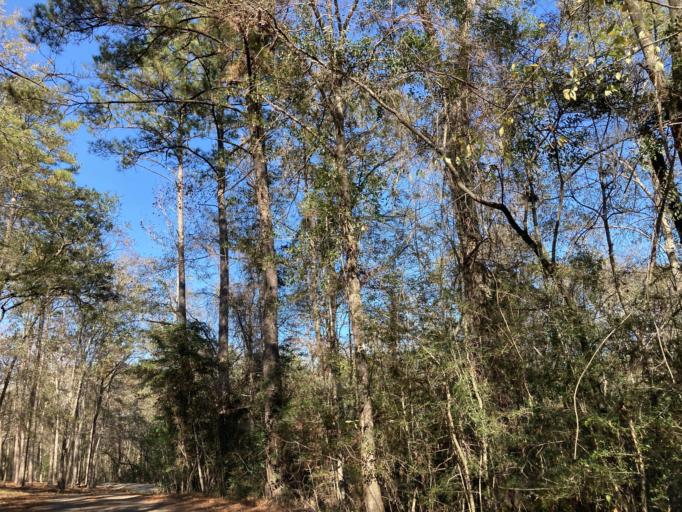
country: US
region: Mississippi
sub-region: Forrest County
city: Petal
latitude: 31.3294
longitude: -89.1670
